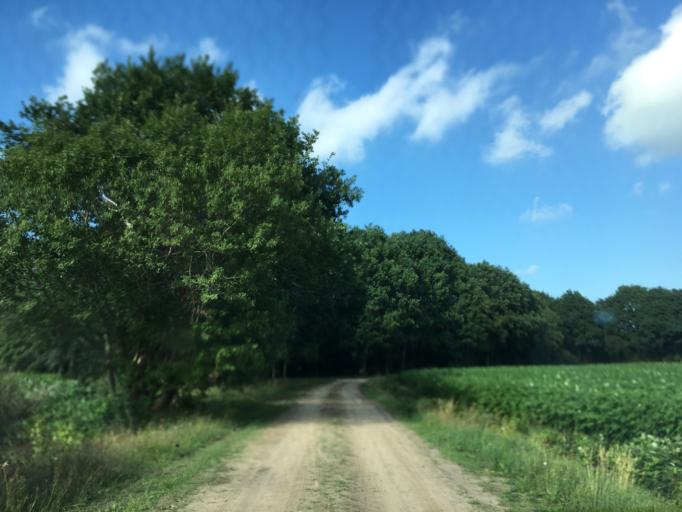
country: NL
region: Drenthe
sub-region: Gemeente Westerveld
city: Dwingeloo
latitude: 52.8619
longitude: 6.3113
